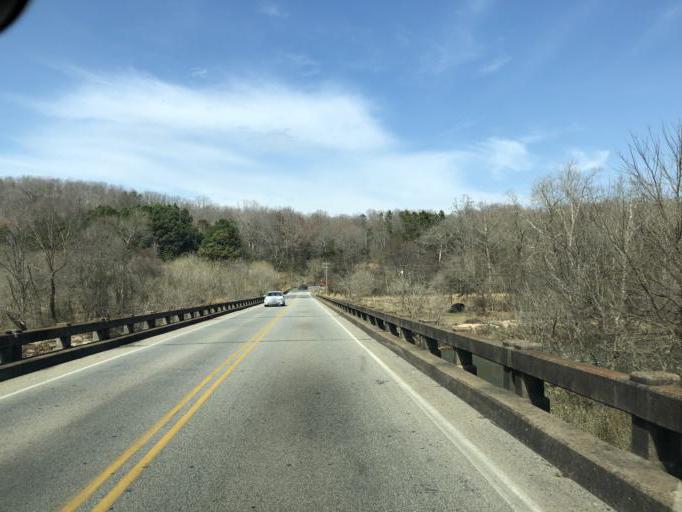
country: US
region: North Carolina
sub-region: Gaston County
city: Ranlo
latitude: 35.3080
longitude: -81.1068
